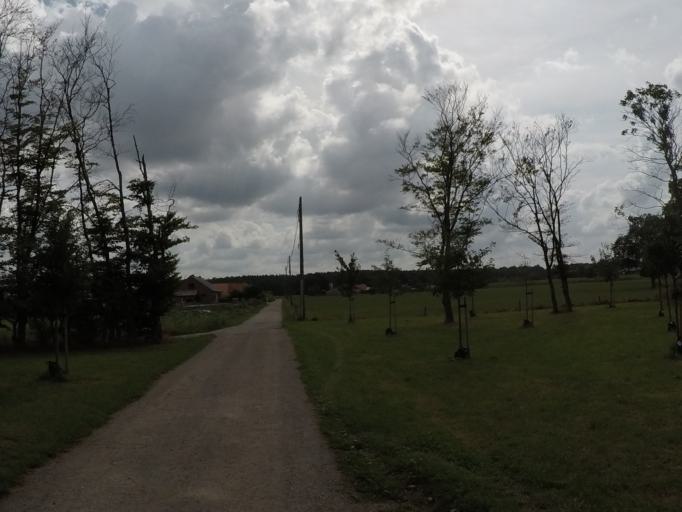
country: BE
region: Flanders
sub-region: Provincie Antwerpen
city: Grobbendonk
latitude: 51.2129
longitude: 4.7334
